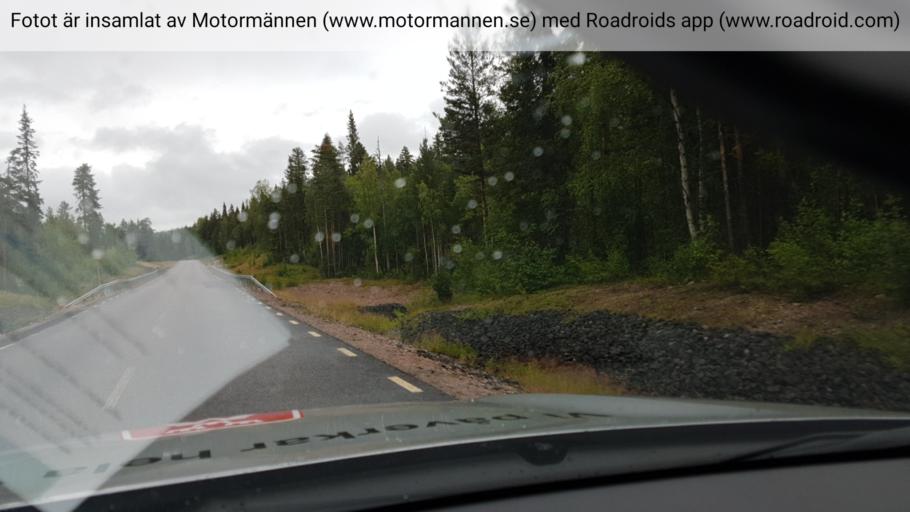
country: SE
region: Norrbotten
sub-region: Gallivare Kommun
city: Gaellivare
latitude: 66.5910
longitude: 20.4698
